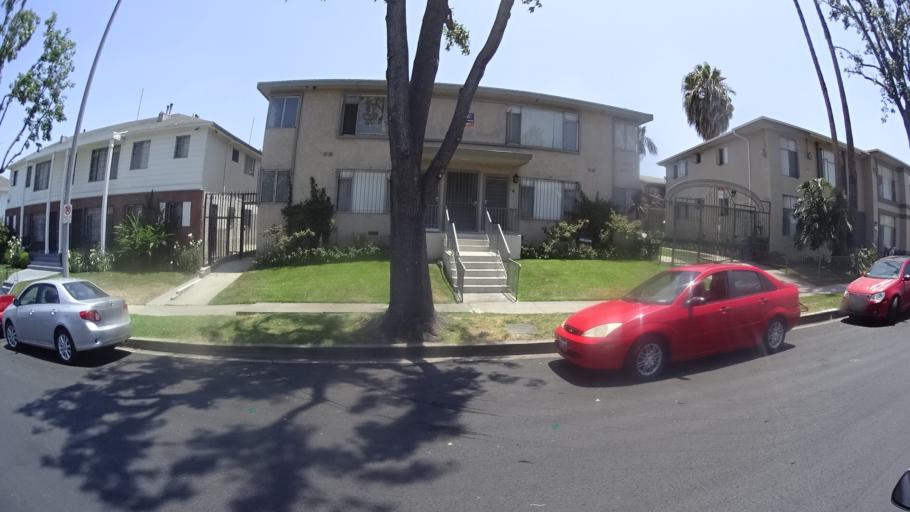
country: US
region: California
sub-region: Los Angeles County
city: View Park-Windsor Hills
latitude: 34.0153
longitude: -118.3465
